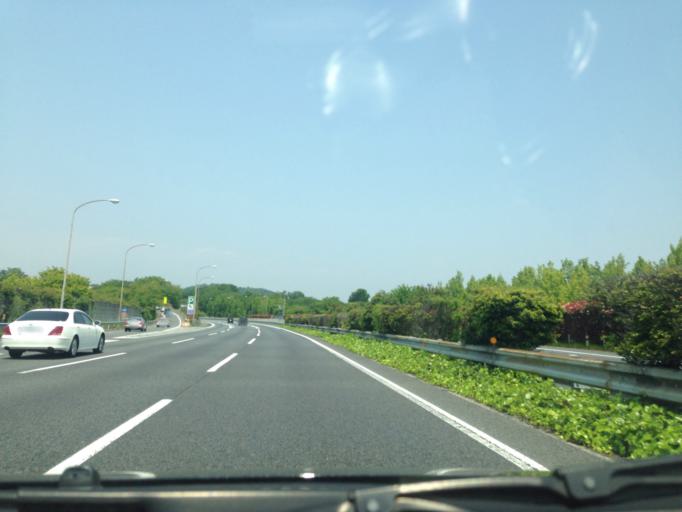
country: JP
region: Tochigi
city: Sano
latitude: 36.3142
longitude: 139.6212
